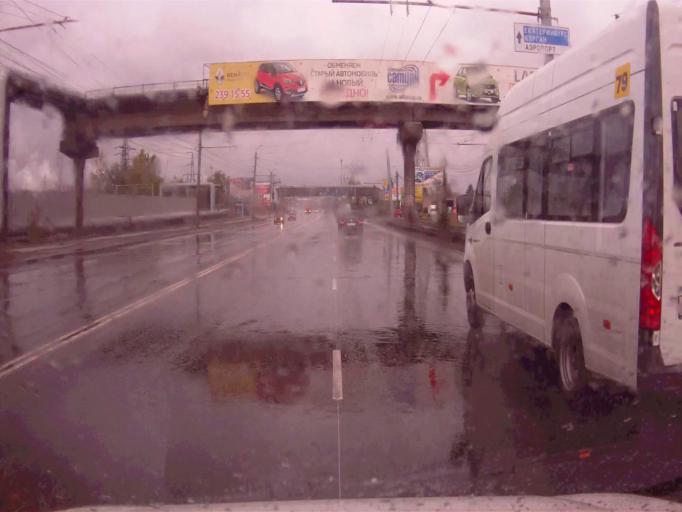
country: RU
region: Chelyabinsk
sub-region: Gorod Chelyabinsk
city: Chelyabinsk
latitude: 55.2032
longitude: 61.3854
